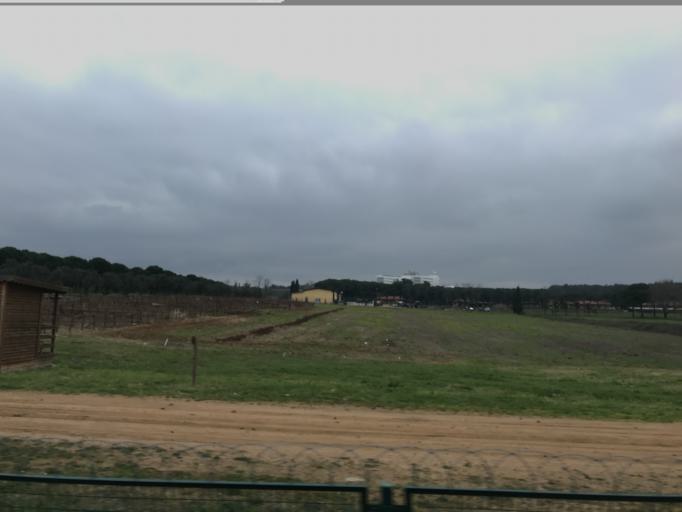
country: TR
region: Kocaeli
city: Darica
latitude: 40.8105
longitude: 29.3501
